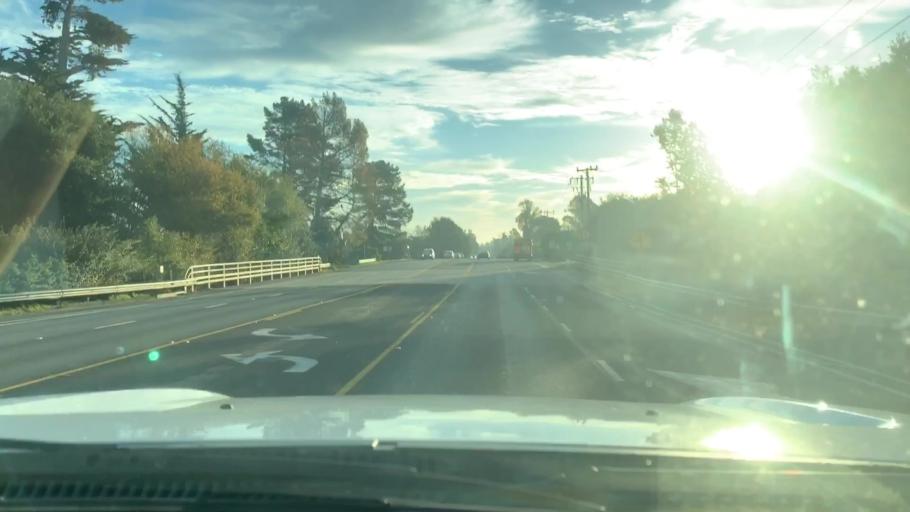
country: US
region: California
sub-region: San Luis Obispo County
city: Los Osos
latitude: 35.3061
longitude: -120.8122
